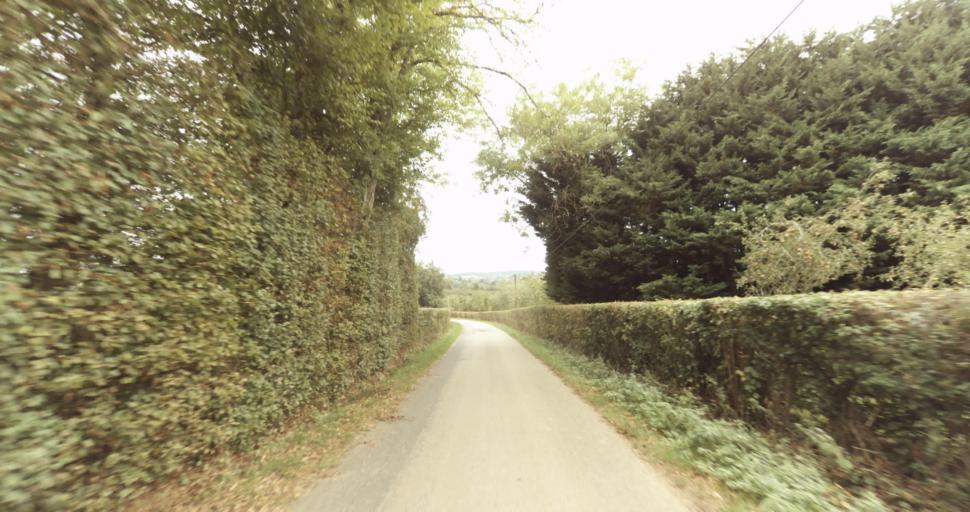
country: FR
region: Lower Normandy
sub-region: Departement de l'Orne
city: Gace
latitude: 48.7449
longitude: 0.3373
